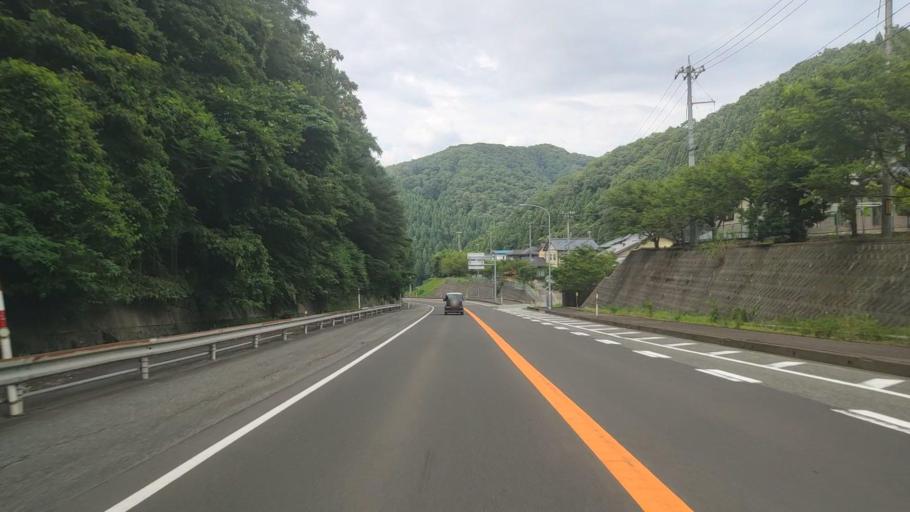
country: JP
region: Fukui
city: Takefu
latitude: 35.8134
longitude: 136.1005
